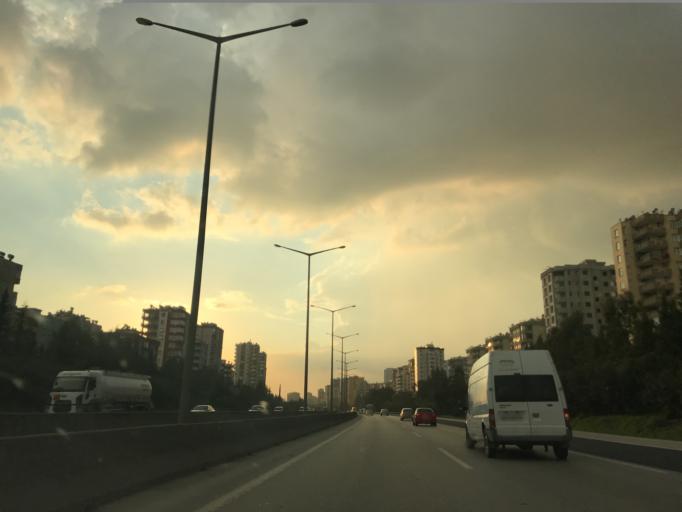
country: TR
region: Adana
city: Adana
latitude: 37.0329
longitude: 35.3000
